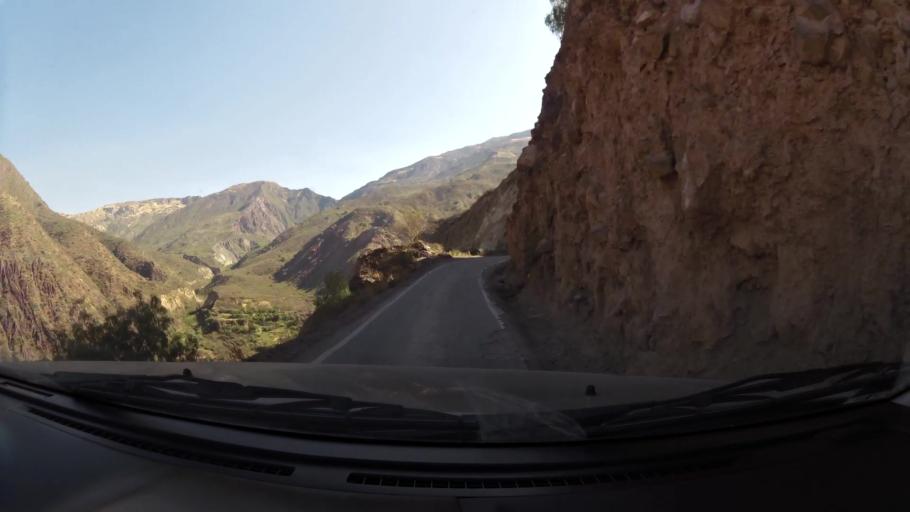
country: PE
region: Huancavelica
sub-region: Provincia de Acobamba
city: Pomacocha
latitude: -12.7858
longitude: -74.4940
